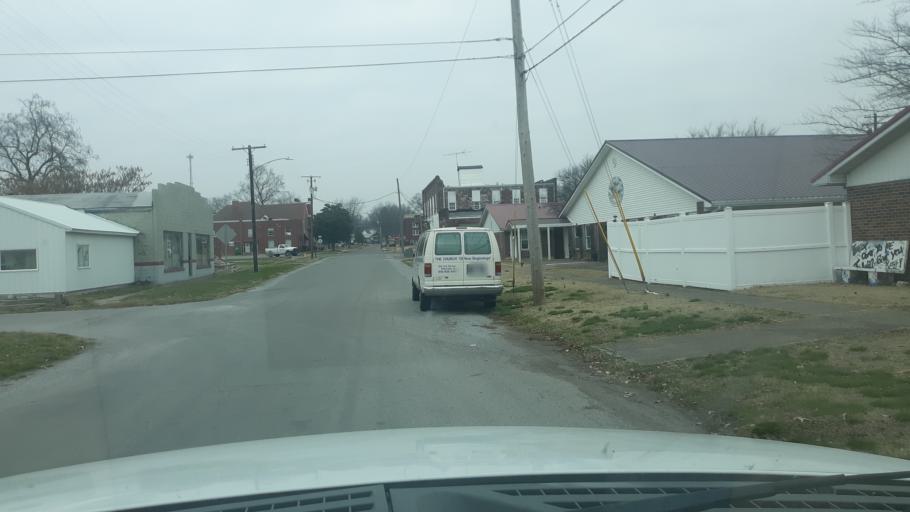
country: US
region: Illinois
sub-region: Saline County
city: Eldorado
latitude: 37.8123
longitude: -88.4386
